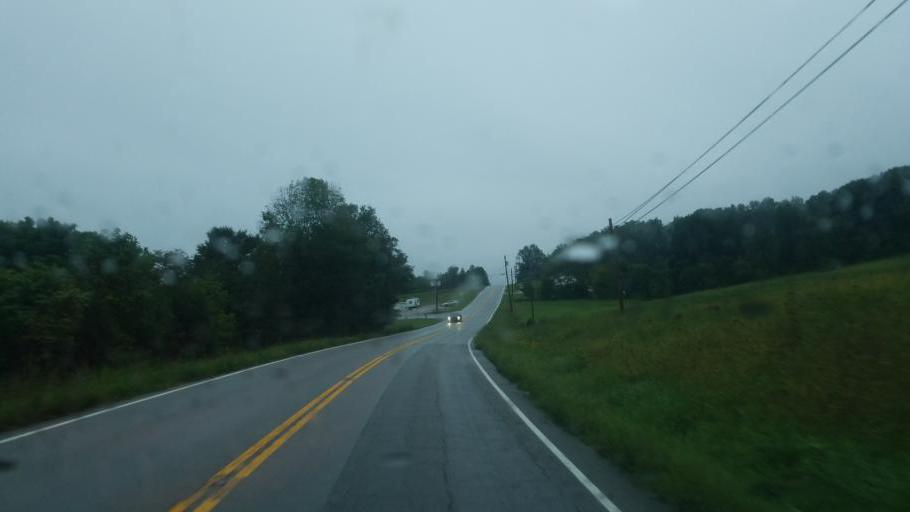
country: US
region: Kentucky
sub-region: Fleming County
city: Flemingsburg
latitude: 38.3836
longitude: -83.6516
